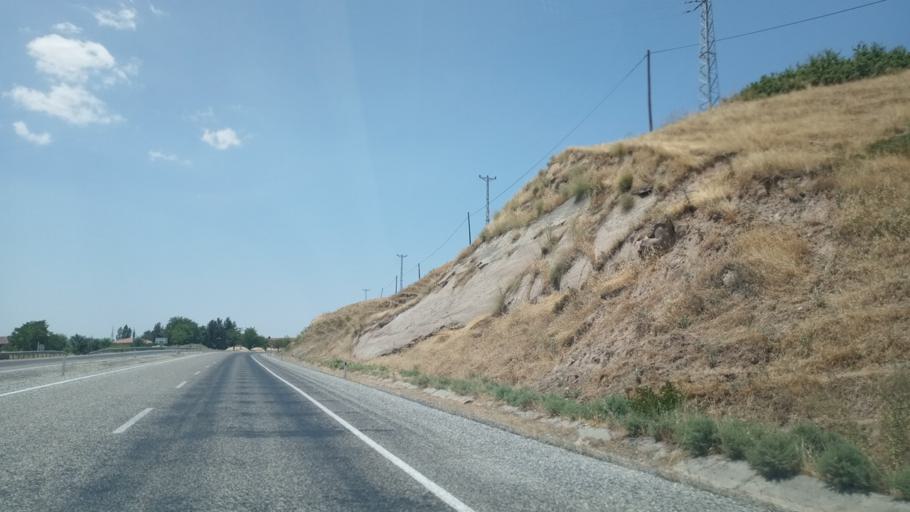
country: TR
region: Batman
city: Bekirhan
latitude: 38.1570
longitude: 41.3334
